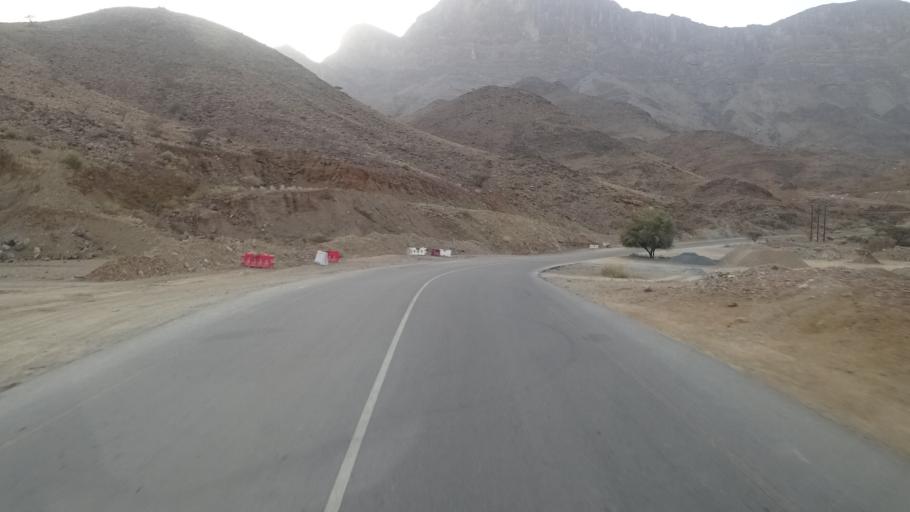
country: OM
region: Muhafazat ad Dakhiliyah
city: Bahla'
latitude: 23.1859
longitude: 57.1397
